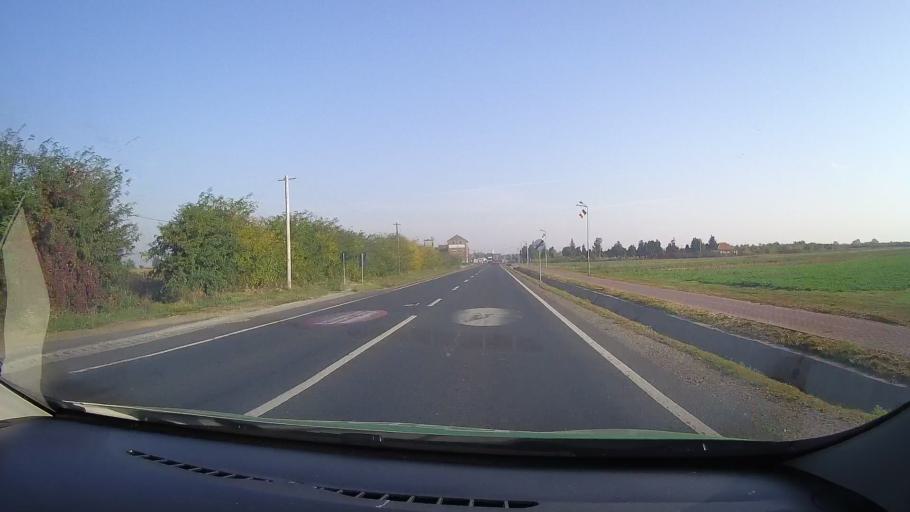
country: RO
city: Chisineu-Cris
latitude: 46.5083
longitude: 21.5074
